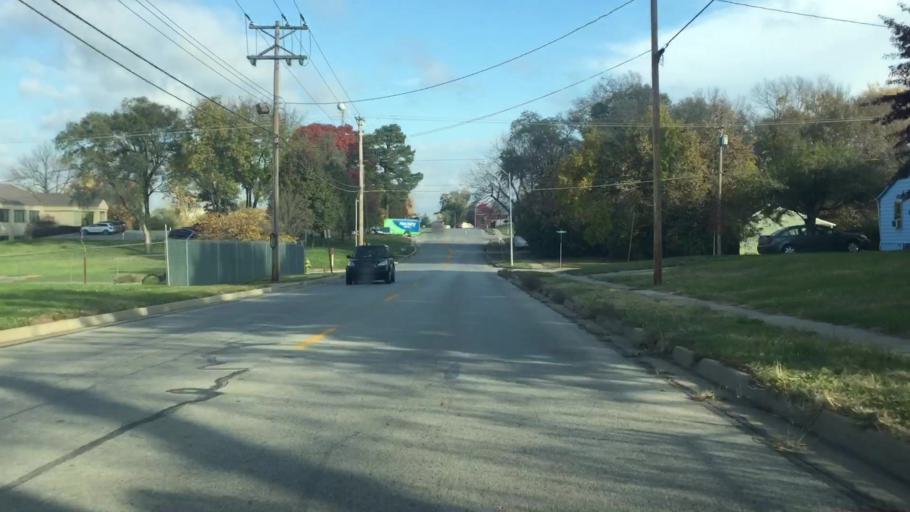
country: US
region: Missouri
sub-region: Jackson County
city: Grandview
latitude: 38.8872
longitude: -94.5397
